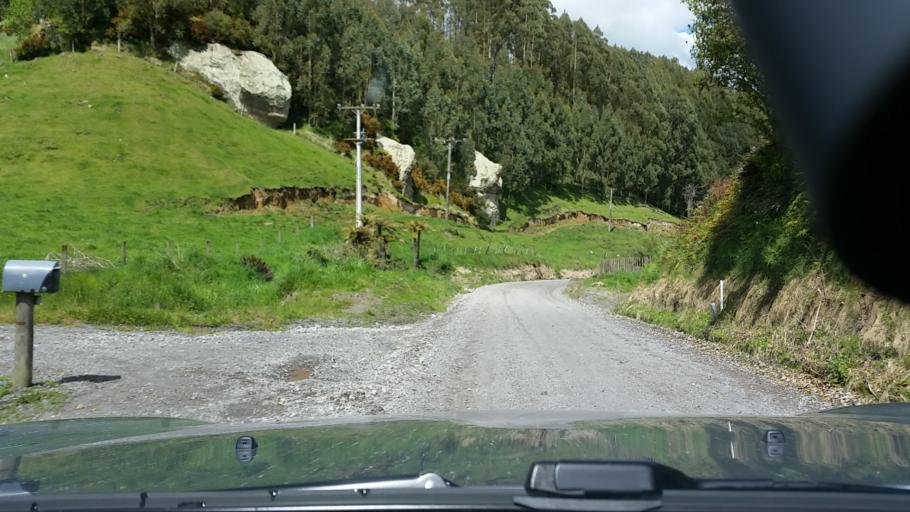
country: NZ
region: Bay of Plenty
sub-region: Rotorua District
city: Rotorua
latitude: -38.3798
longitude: 176.1182
